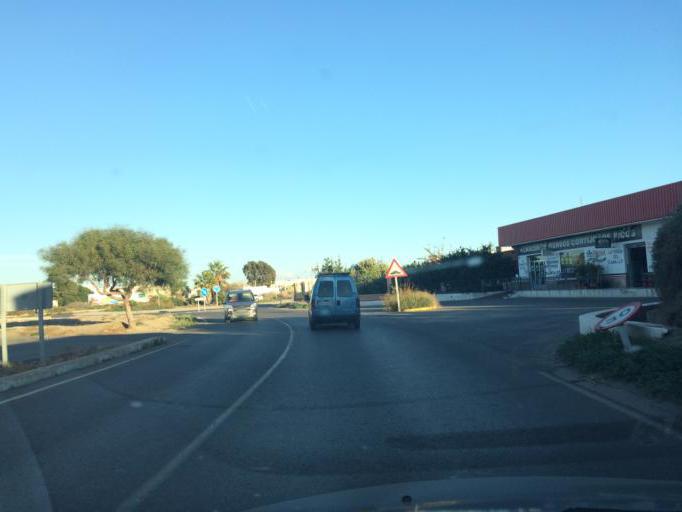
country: ES
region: Andalusia
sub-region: Provincia de Almeria
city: Almeria
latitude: 36.8395
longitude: -2.4189
